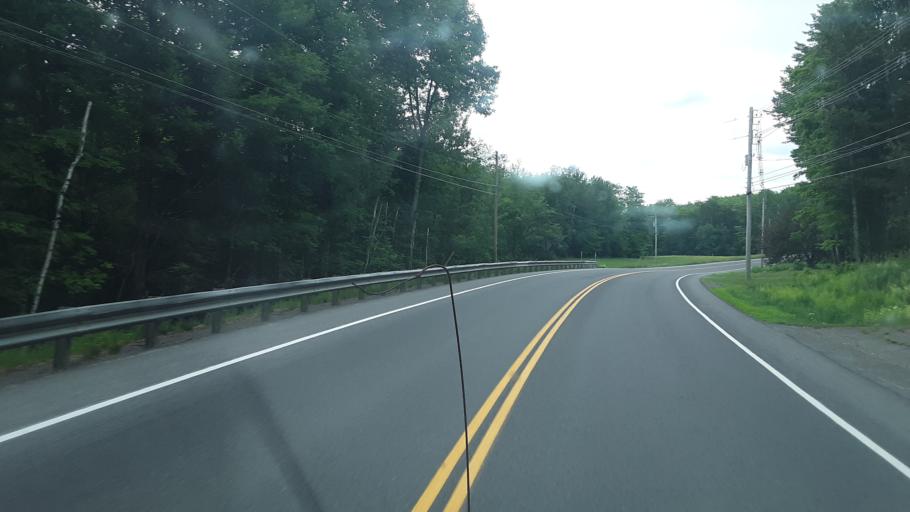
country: US
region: Maine
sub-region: Penobscot County
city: Patten
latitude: 45.8857
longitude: -68.4185
